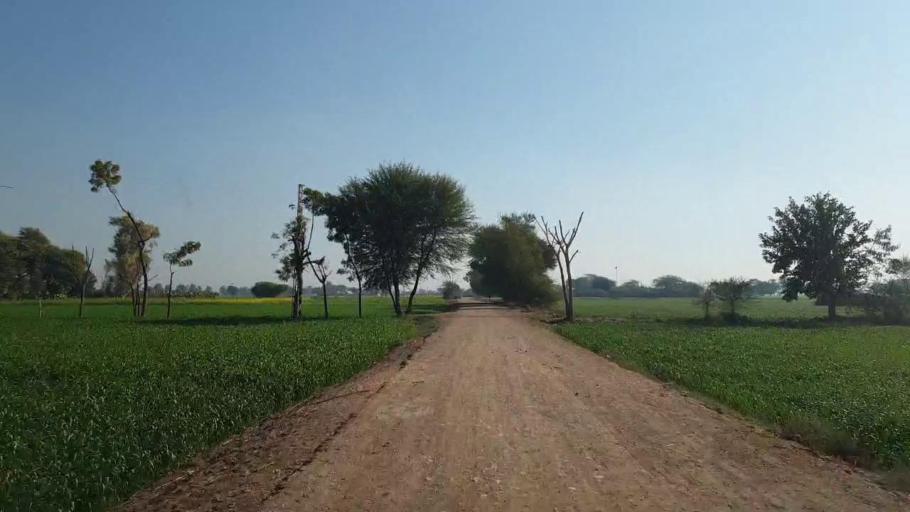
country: PK
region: Sindh
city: Shahpur Chakar
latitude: 26.0609
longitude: 68.4836
